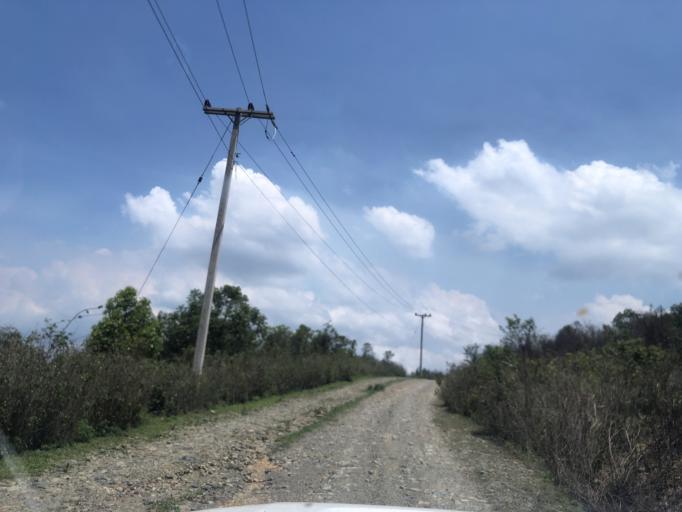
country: LA
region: Phongsali
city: Phongsali
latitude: 21.4208
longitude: 102.1842
